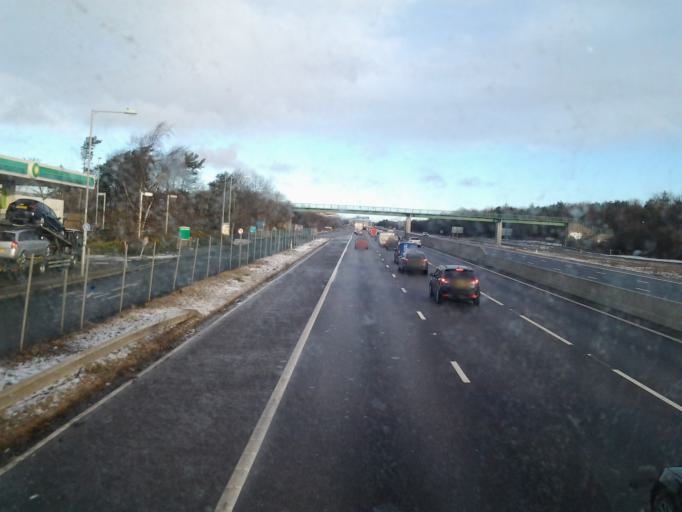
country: GB
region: England
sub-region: County Durham
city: Chester-le-Street
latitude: 54.8899
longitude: -1.5594
